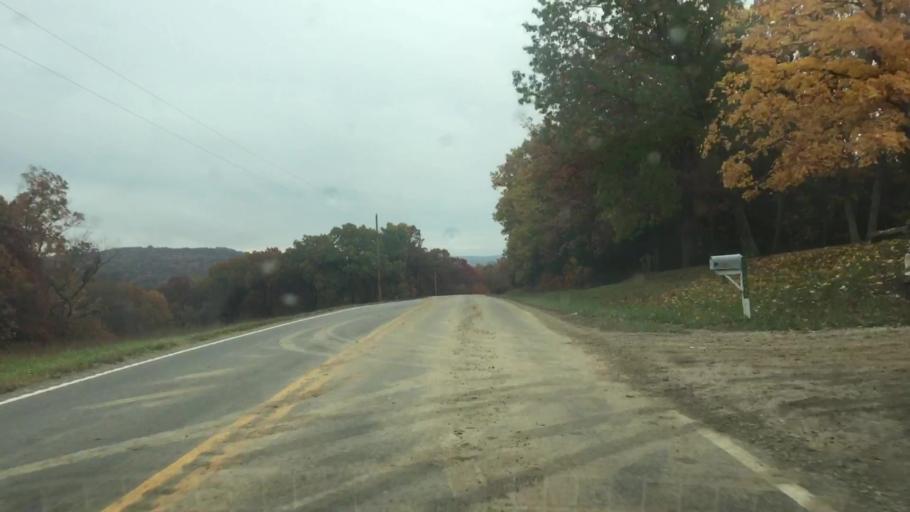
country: US
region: Missouri
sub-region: Gasconade County
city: Hermann
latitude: 38.7147
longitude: -91.6390
